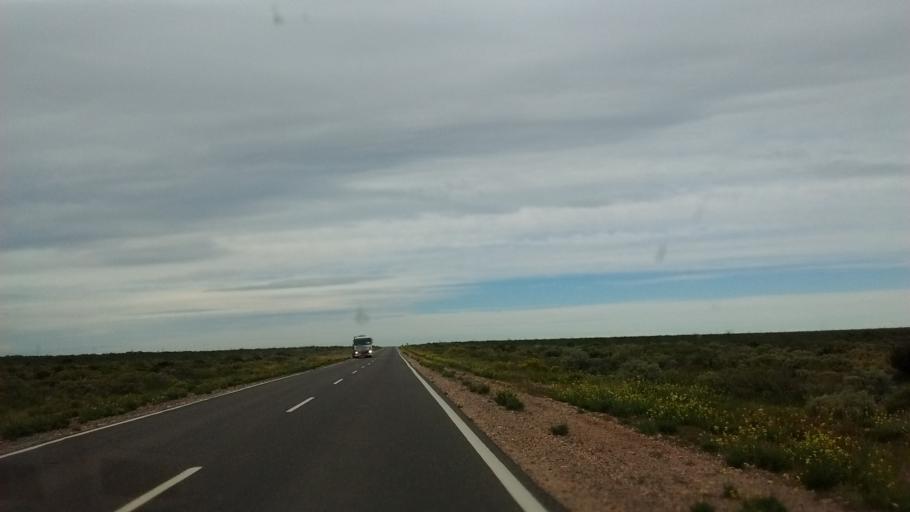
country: AR
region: Rio Negro
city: Contraalmirante Cordero
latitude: -38.3594
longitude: -68.0172
